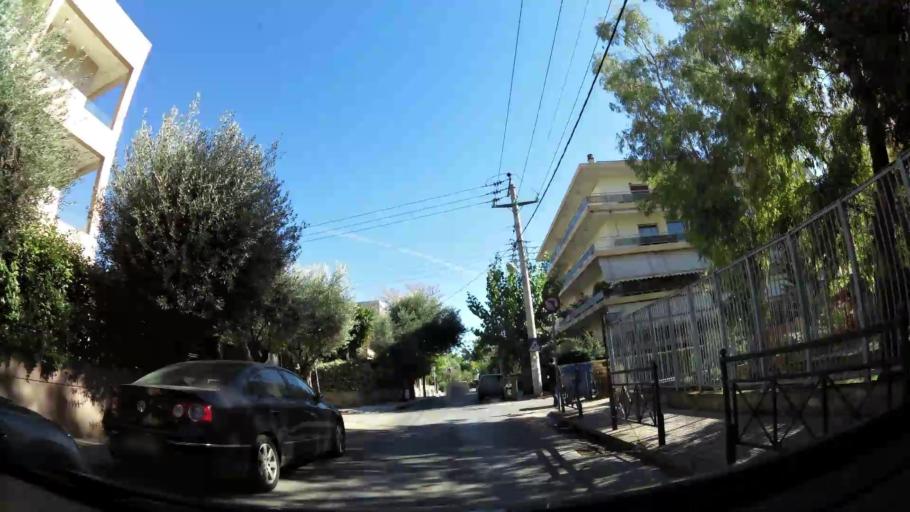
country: GR
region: Attica
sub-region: Nomarchia Athinas
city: Khalandrion
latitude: 38.0279
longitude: 23.8152
